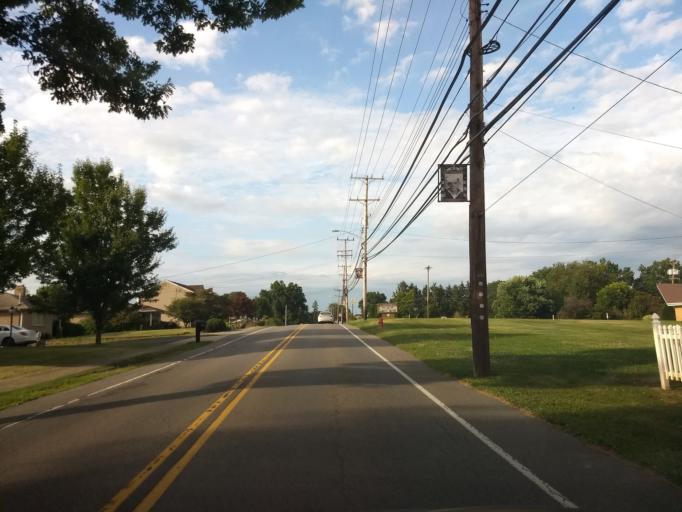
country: US
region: Pennsylvania
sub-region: Allegheny County
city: Emsworth
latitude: 40.4748
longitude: -80.1325
